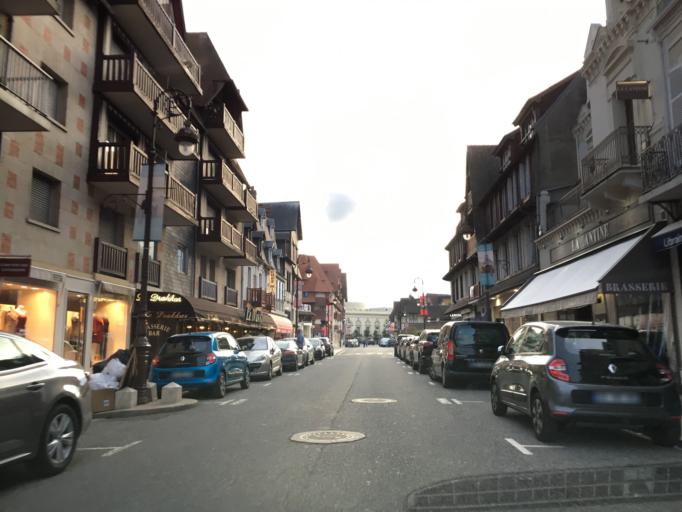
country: FR
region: Lower Normandy
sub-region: Departement du Calvados
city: Deauville
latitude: 49.3595
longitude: 0.0737
